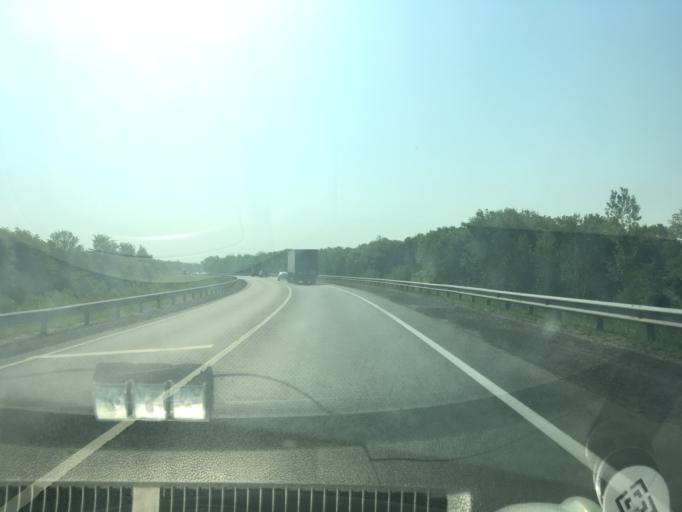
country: RU
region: Nizjnij Novgorod
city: Kstovo
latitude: 56.0960
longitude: 44.3129
